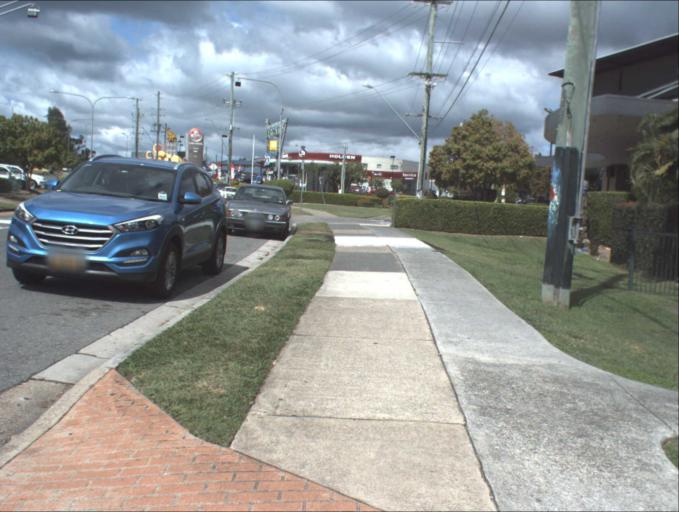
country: AU
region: Queensland
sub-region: Logan
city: Park Ridge South
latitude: -27.6681
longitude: 153.0323
